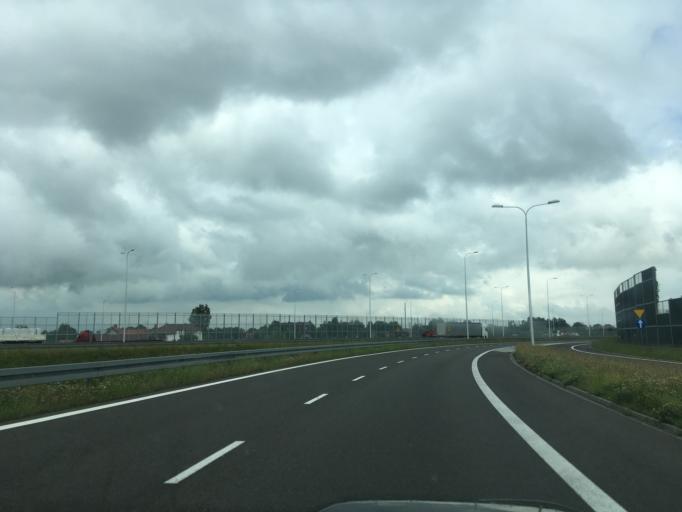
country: PL
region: Lublin Voivodeship
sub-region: Powiat lubelski
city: Jastkow
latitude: 51.2855
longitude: 22.4565
